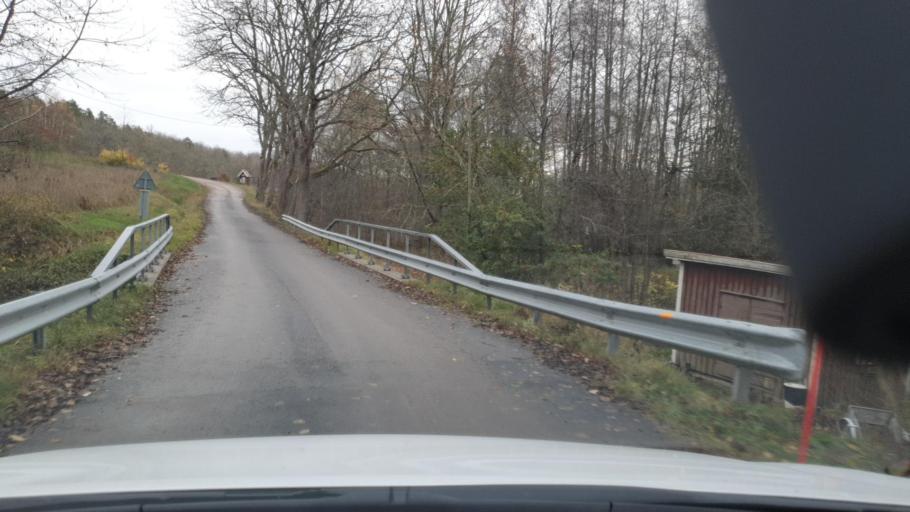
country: SE
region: Kalmar
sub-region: Vasterviks Kommun
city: Vaestervik
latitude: 57.7353
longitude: 16.4858
